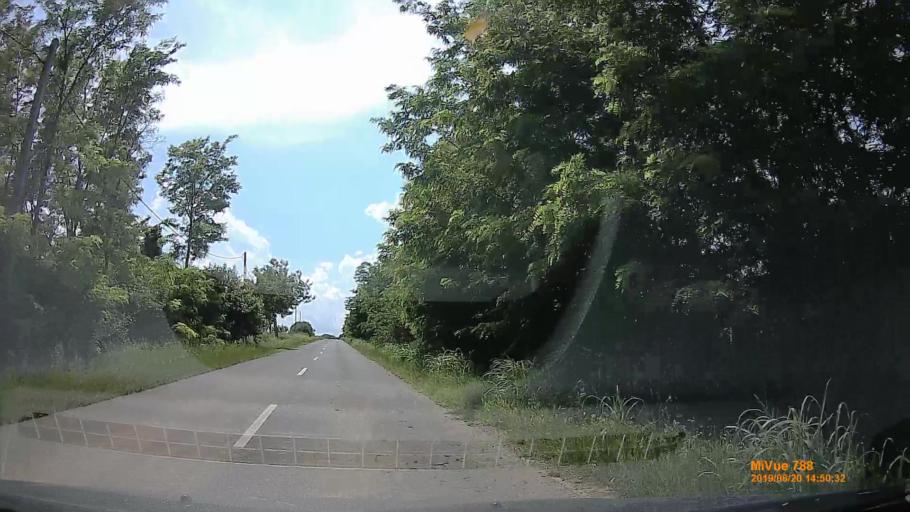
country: HU
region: Baranya
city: Kozarmisleny
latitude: 46.0143
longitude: 18.2625
